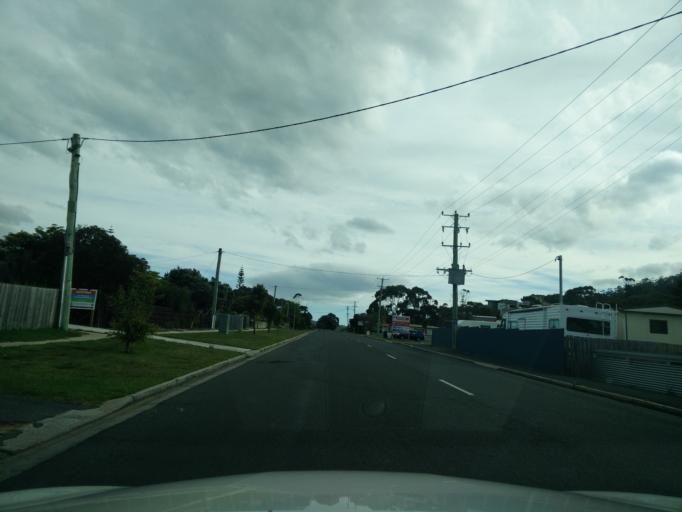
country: AU
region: Tasmania
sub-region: Break O'Day
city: St Helens
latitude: -41.8770
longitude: 148.3038
